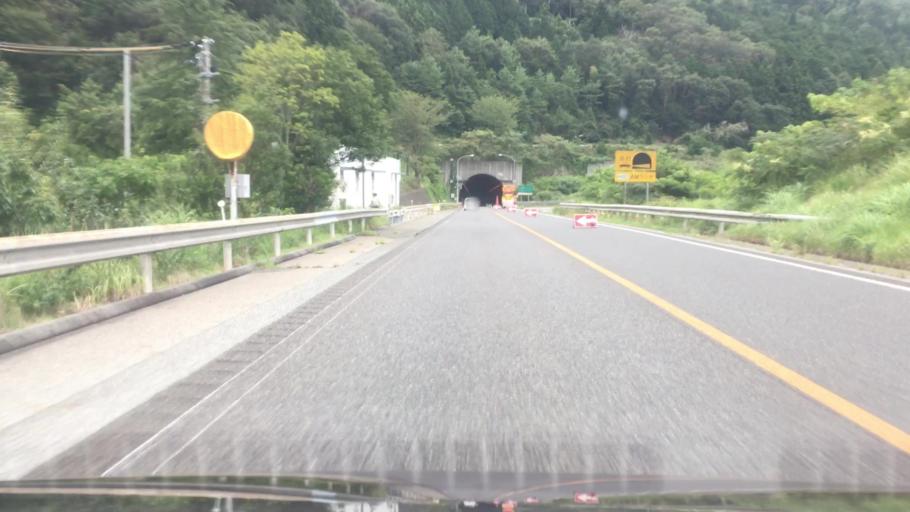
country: JP
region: Hyogo
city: Sasayama
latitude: 35.1146
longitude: 135.1652
